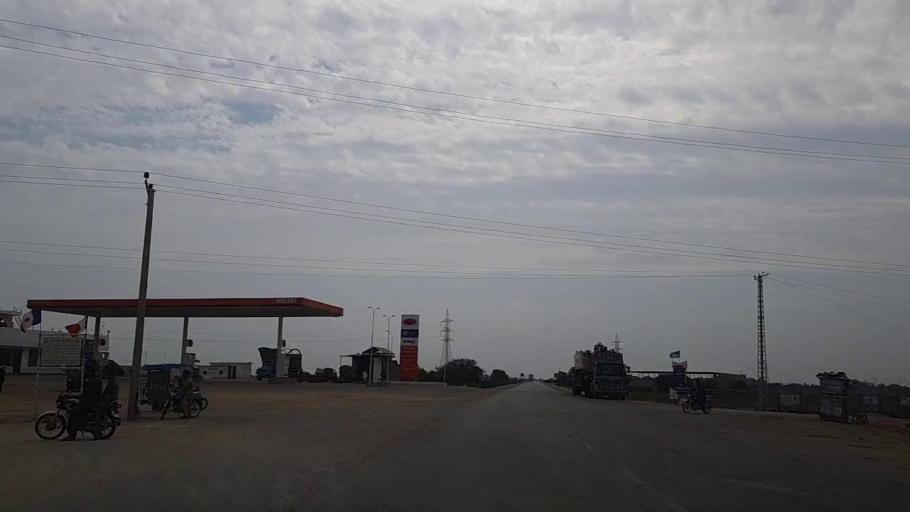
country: PK
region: Sindh
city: Daro Mehar
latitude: 24.6147
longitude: 68.0892
